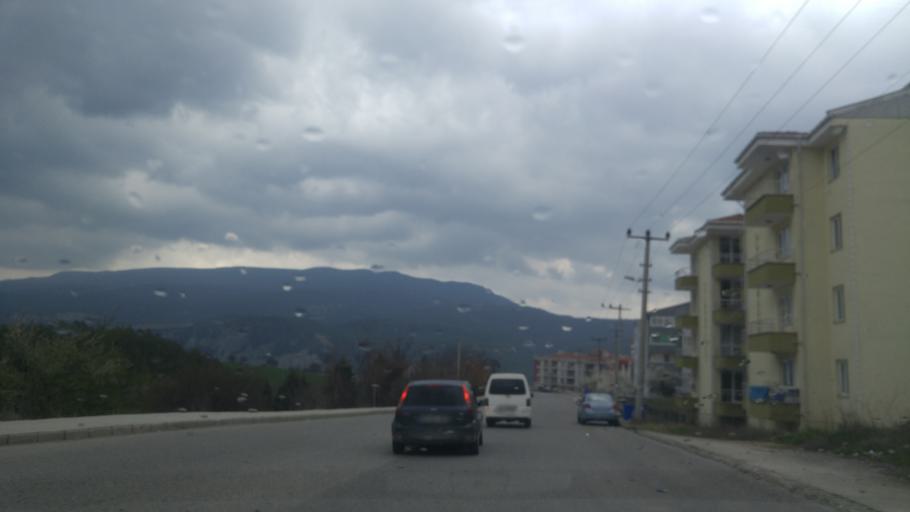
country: TR
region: Karabuk
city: Safranbolu
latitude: 41.2240
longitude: 32.6720
